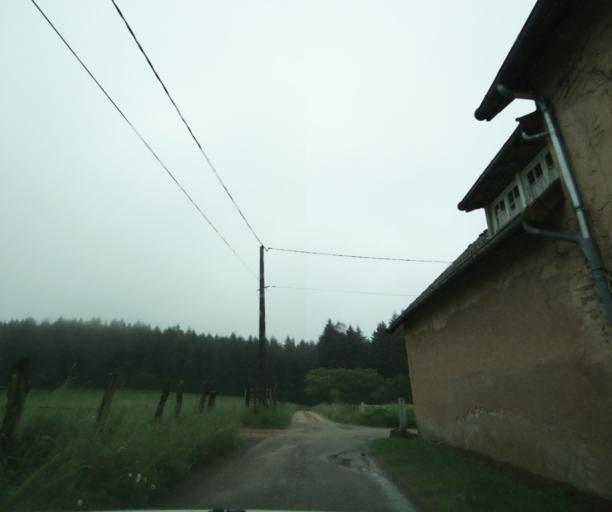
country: FR
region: Bourgogne
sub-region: Departement de Saone-et-Loire
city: Charolles
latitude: 46.3887
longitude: 4.3737
